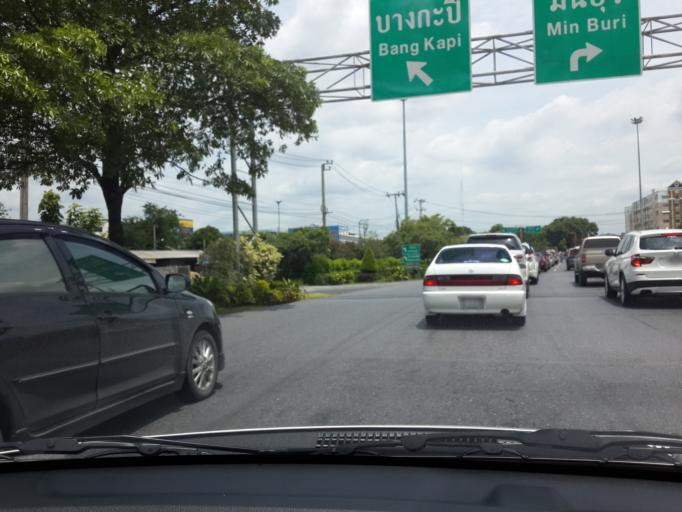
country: TH
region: Bangkok
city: Saphan Sung
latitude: 13.7806
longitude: 100.6836
